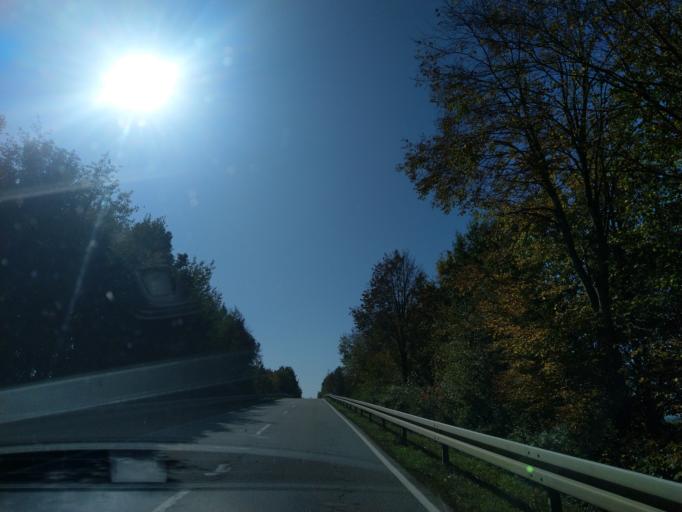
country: DE
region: Bavaria
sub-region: Lower Bavaria
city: Stephansposching
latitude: 48.8067
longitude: 12.8010
